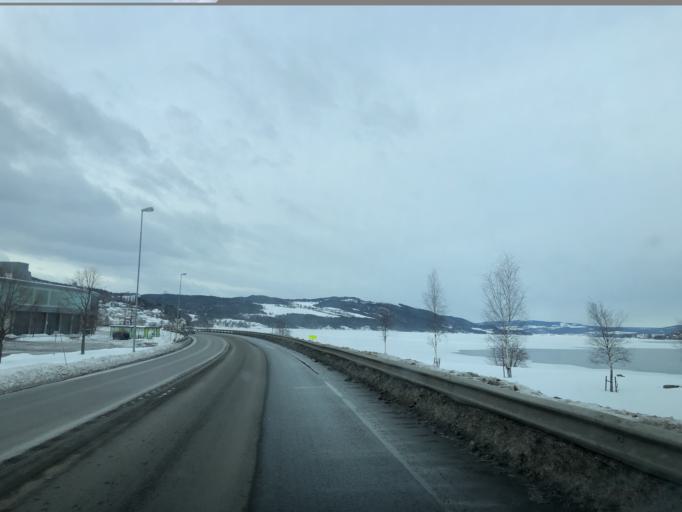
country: NO
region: Oppland
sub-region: Gjovik
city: Gjovik
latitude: 60.7990
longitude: 10.6960
